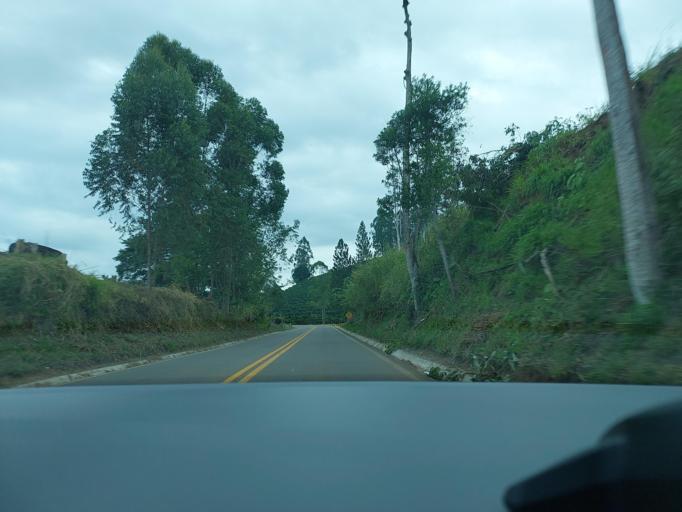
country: BR
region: Minas Gerais
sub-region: Mirai
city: Mirai
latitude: -20.9996
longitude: -42.5495
